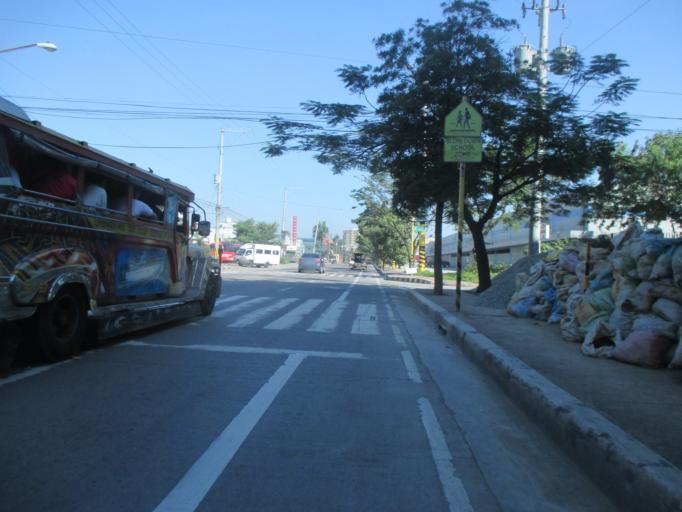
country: PH
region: Metro Manila
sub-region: Marikina
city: Calumpang
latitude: 14.6295
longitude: 121.1019
